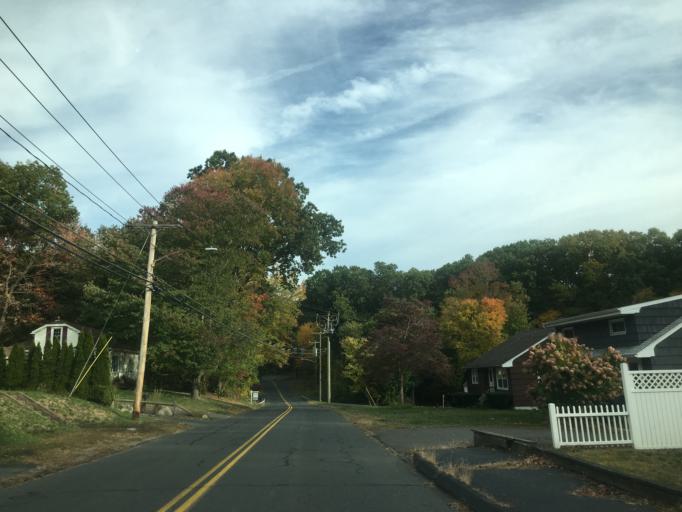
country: US
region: Connecticut
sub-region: Hartford County
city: Sherwood Manor
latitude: 42.0239
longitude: -72.5803
